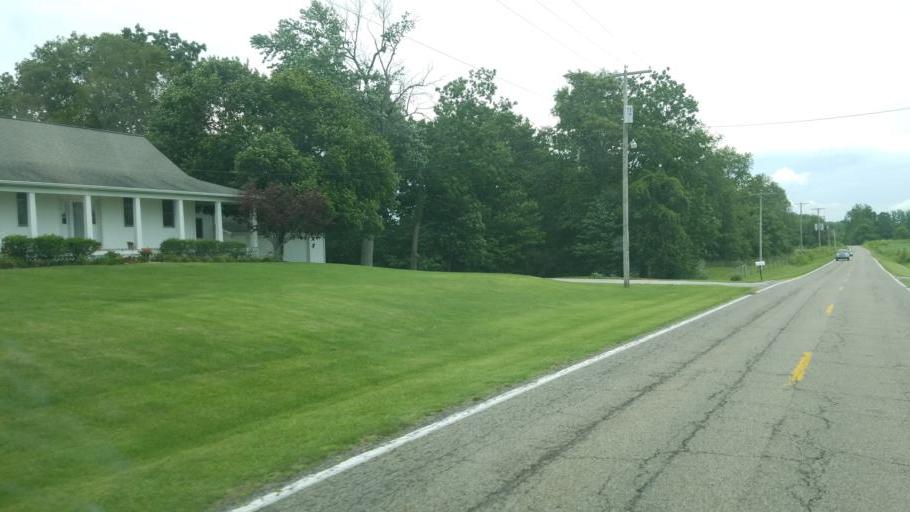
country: US
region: Ohio
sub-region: Licking County
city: Utica
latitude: 40.2543
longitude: -82.5453
